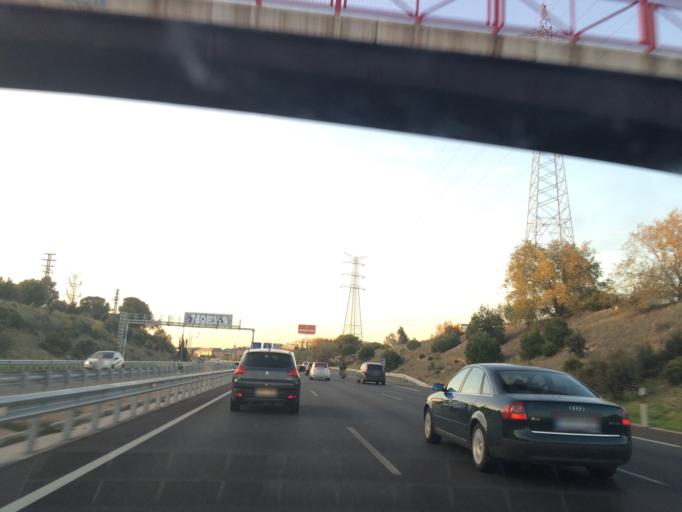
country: ES
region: Madrid
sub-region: Provincia de Madrid
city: Majadahonda
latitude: 40.4455
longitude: -3.8528
